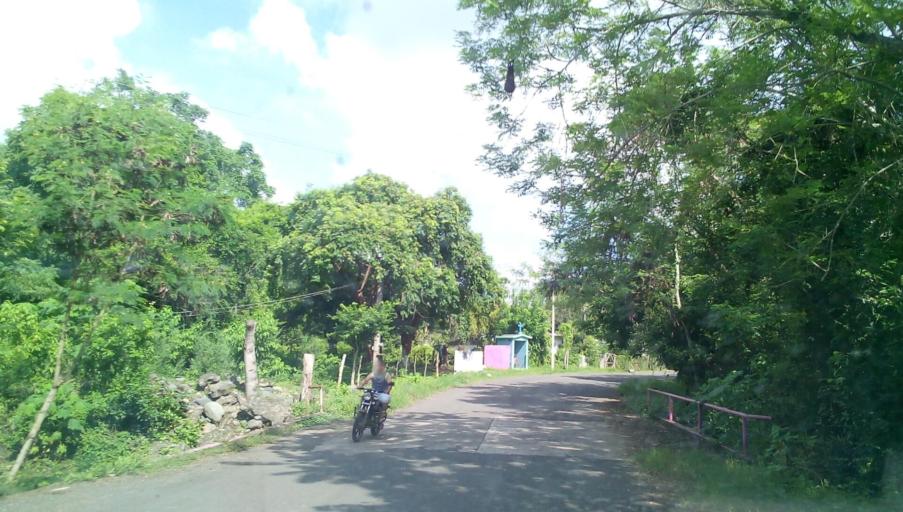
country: MX
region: Veracruz
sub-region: Citlaltepetl
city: Las Sabinas
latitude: 21.3561
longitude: -97.8993
